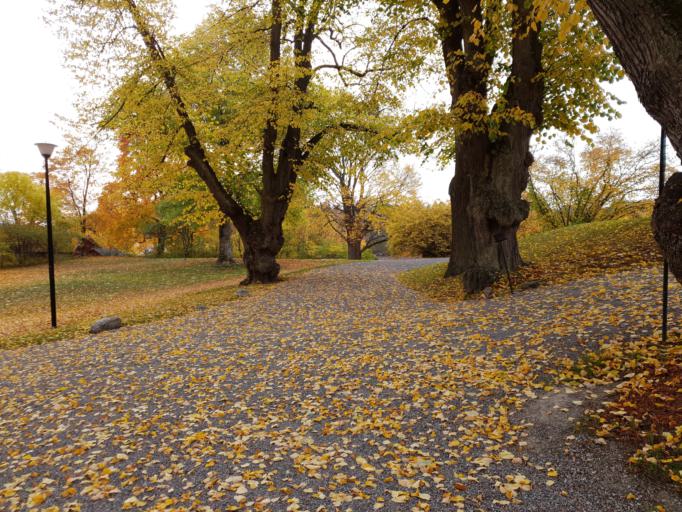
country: SE
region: Stockholm
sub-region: Stockholms Kommun
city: Bromma
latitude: 59.3476
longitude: 17.9009
